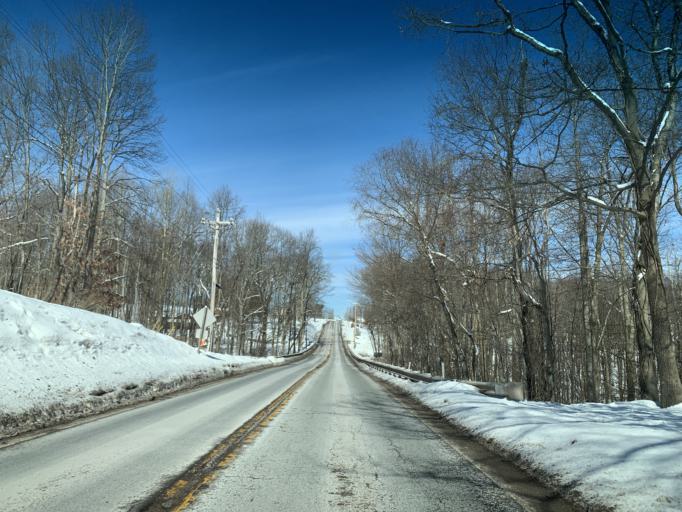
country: US
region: West Virginia
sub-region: Preston County
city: Terra Alta
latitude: 39.6740
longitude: -79.4515
